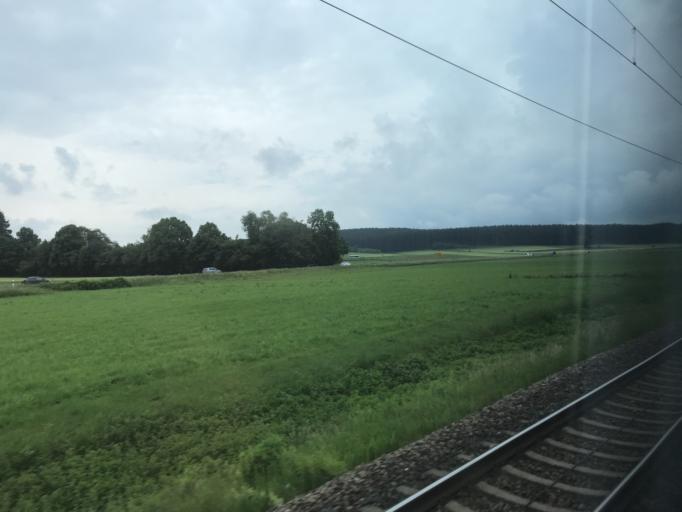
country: DE
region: Bavaria
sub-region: Swabia
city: Diedorf
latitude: 48.3454
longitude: 10.7619
